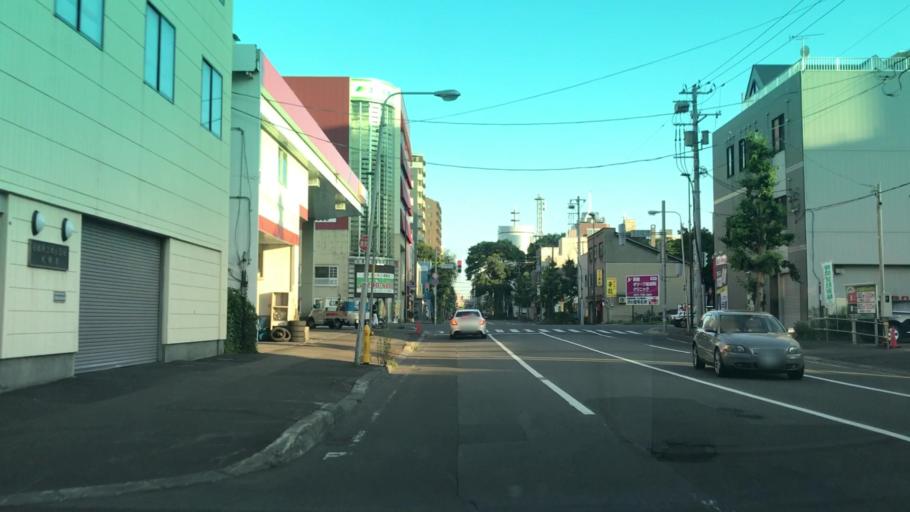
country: JP
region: Hokkaido
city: Sapporo
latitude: 43.0652
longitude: 141.3348
